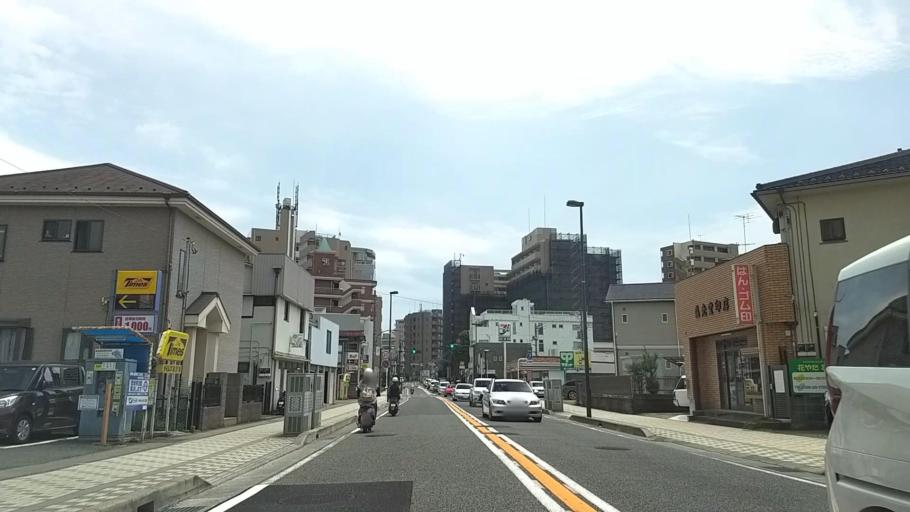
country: JP
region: Kanagawa
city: Fujisawa
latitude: 35.3440
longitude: 139.4876
